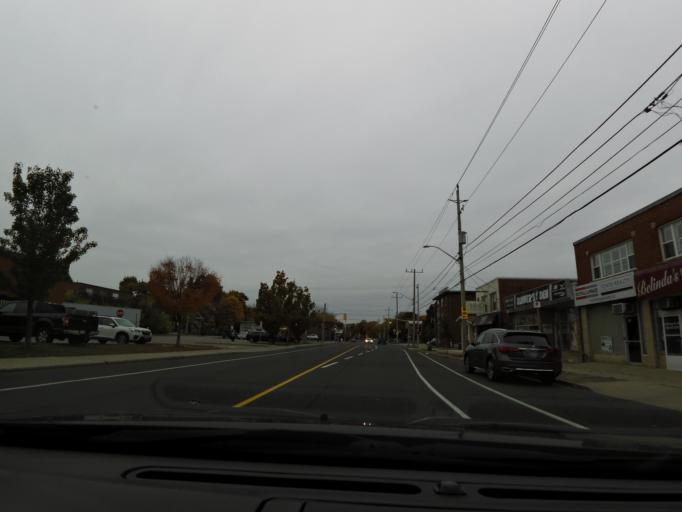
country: CA
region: Ontario
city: Hamilton
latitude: 43.2628
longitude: -79.8998
